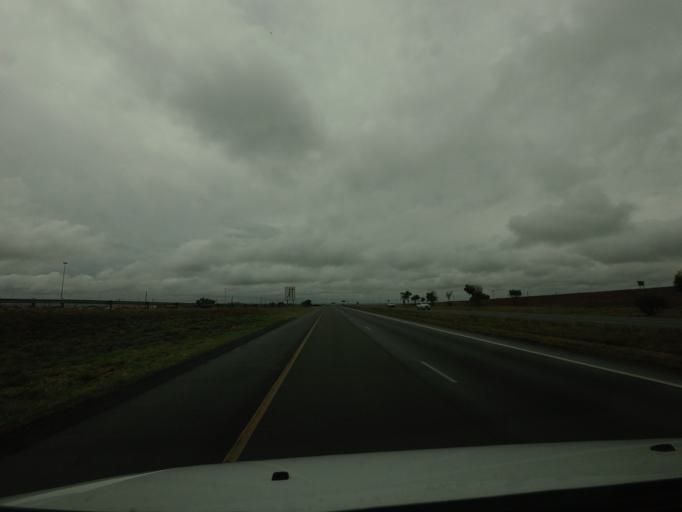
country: ZA
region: Mpumalanga
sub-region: Nkangala District Municipality
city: Middelburg
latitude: -25.8292
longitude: 29.5302
